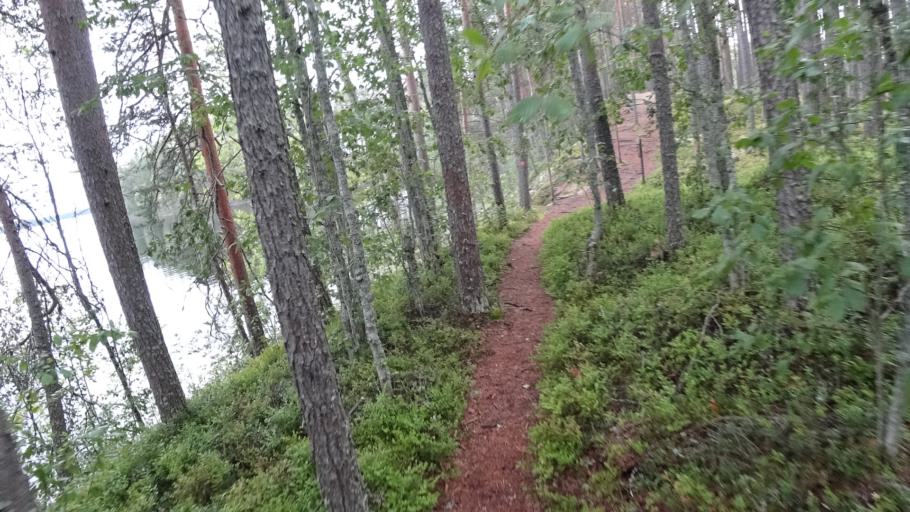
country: FI
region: North Karelia
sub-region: Joensuu
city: Ilomantsi
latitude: 62.5801
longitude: 31.1675
